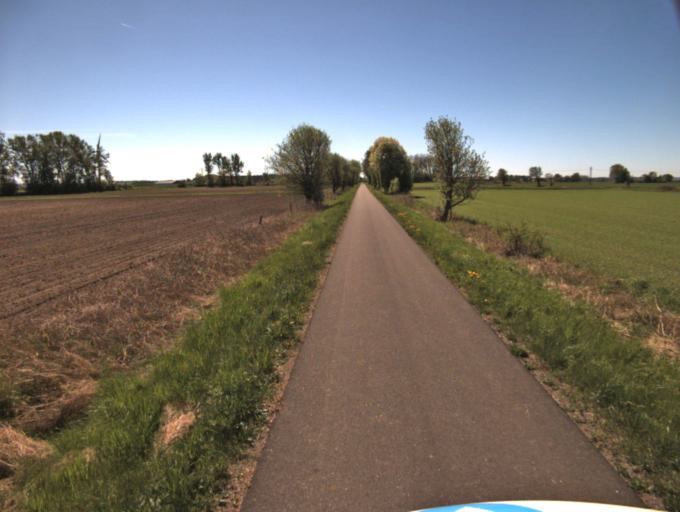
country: SE
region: Skane
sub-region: Kristianstads Kommun
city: Norra Asum
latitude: 55.9641
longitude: 14.1578
